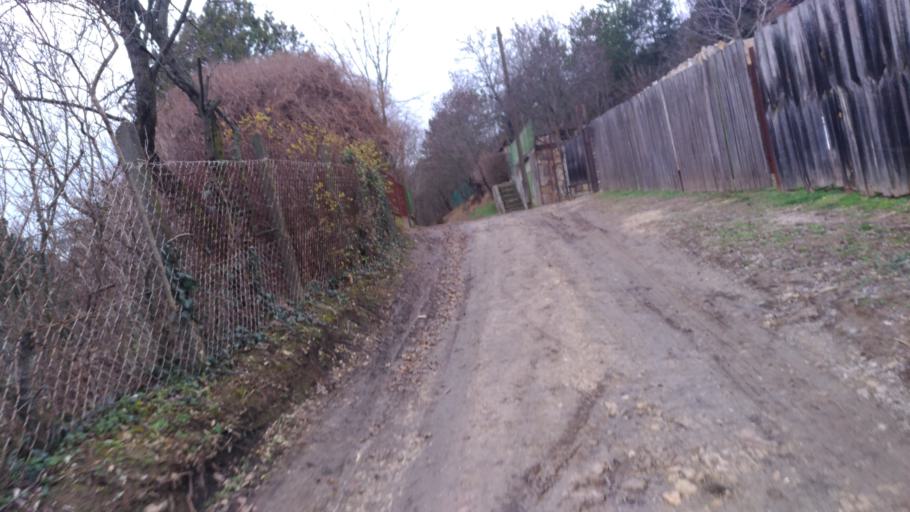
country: HU
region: Pest
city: Urom
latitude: 47.5858
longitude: 19.0225
